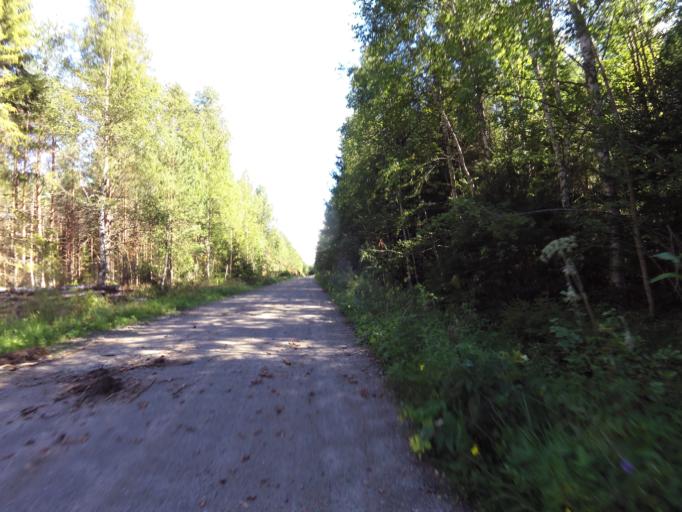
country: SE
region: Gaevleborg
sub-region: Hofors Kommun
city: Hofors
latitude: 60.5126
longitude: 16.3335
